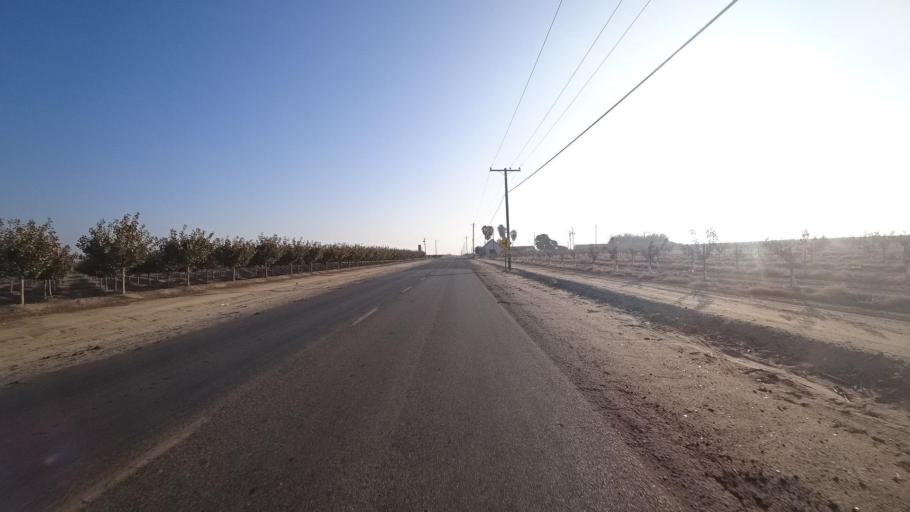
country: US
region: California
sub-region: Tulare County
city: Richgrove
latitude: 35.7907
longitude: -119.1455
